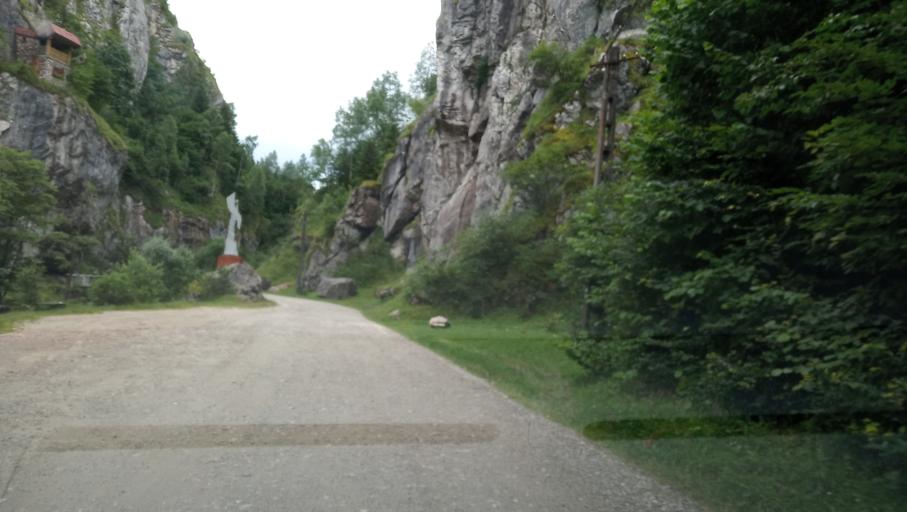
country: RO
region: Hunedoara
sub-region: Oras Petrila
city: Petrila
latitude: 45.4744
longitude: 23.4165
